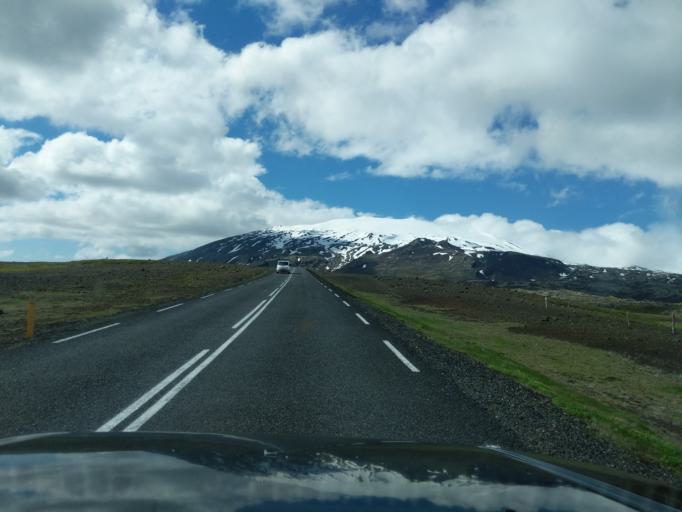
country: IS
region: West
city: Olafsvik
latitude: 64.7529
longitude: -23.6631
